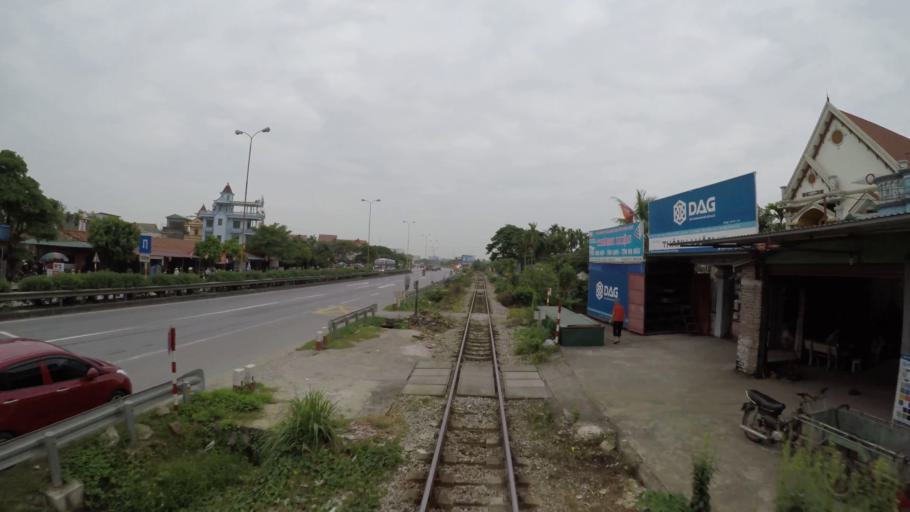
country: VN
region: Hai Duong
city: Phu Thai
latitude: 20.9536
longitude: 106.5301
